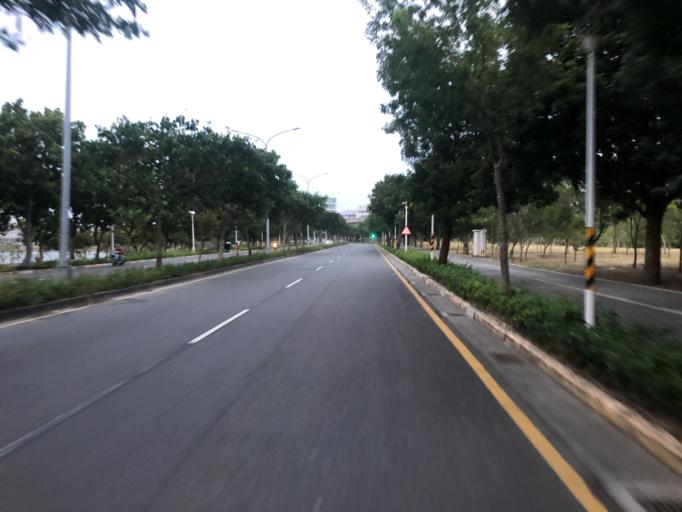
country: TW
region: Taiwan
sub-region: Tainan
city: Tainan
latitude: 23.0850
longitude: 120.2848
